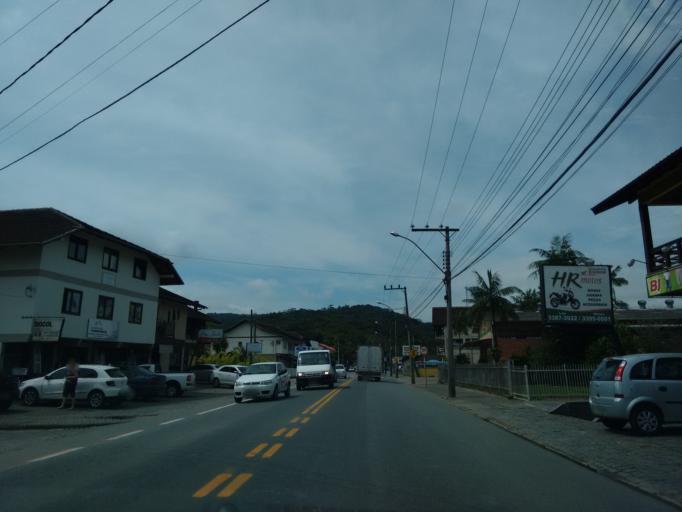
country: BR
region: Santa Catarina
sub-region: Pomerode
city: Pomerode
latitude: -26.7094
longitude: -49.1644
